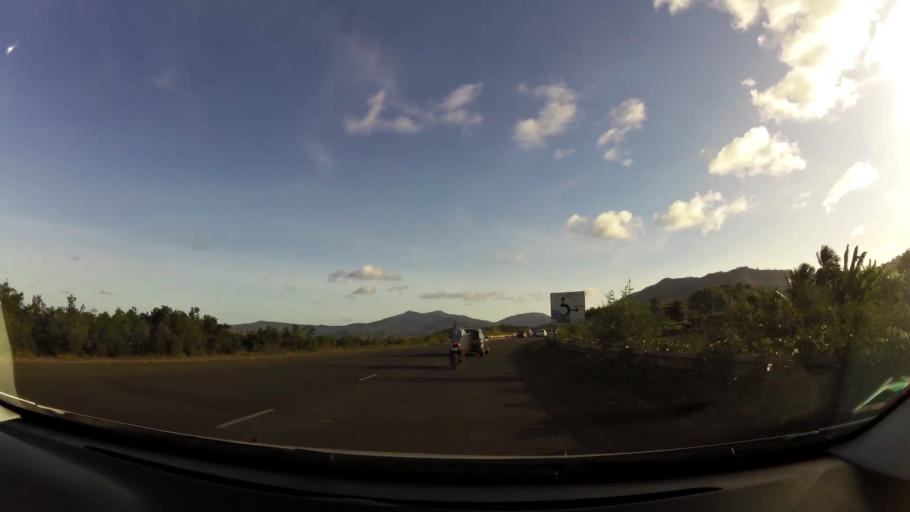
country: YT
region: Mamoudzou
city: Mamoudzou
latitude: -12.8015
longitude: 45.2152
